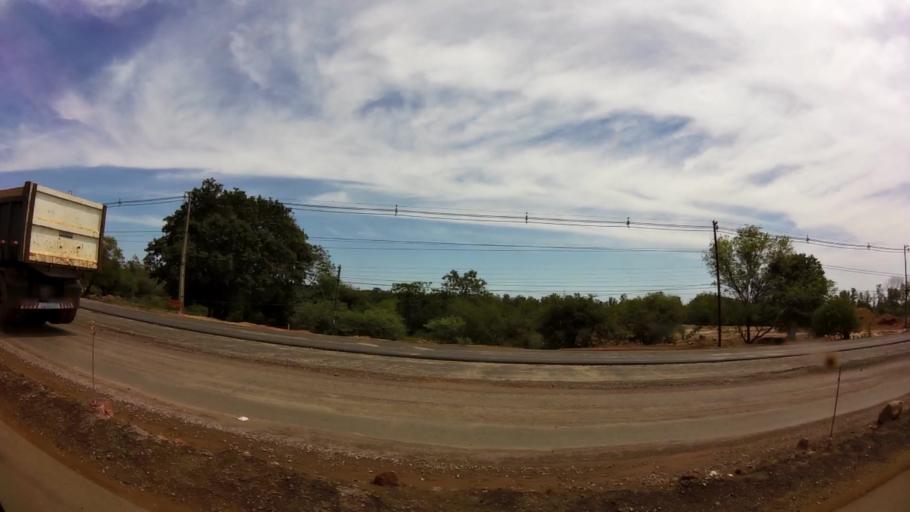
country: PY
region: Central
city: Limpio
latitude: -25.1939
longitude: -57.5084
